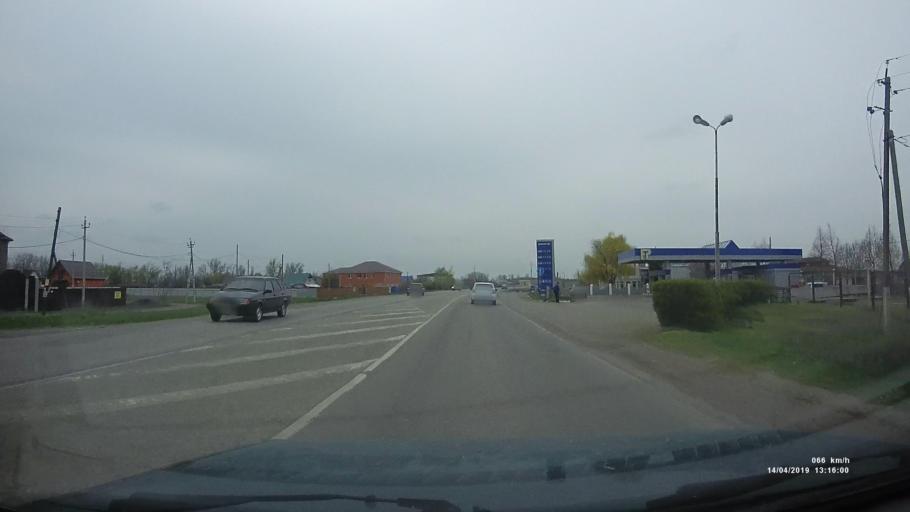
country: RU
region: Rostov
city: Kuleshovka
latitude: 47.0812
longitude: 39.5873
